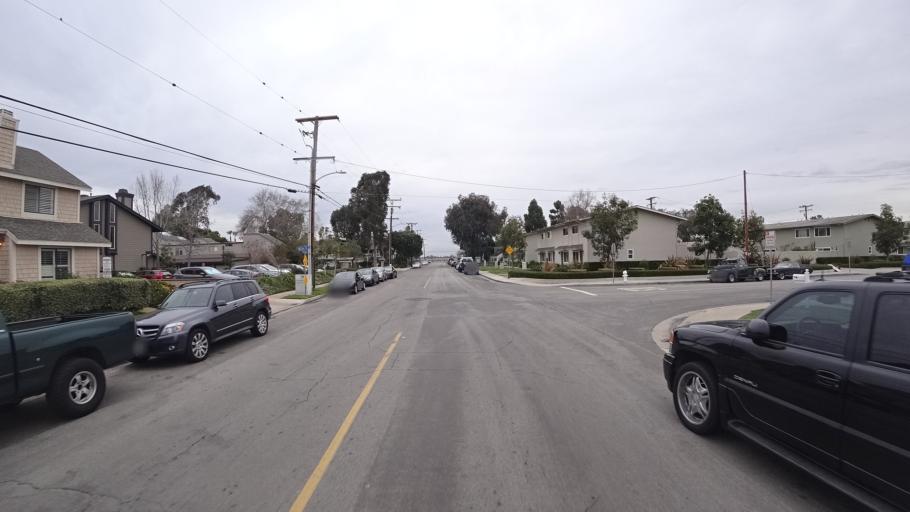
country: US
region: California
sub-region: Orange County
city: Costa Mesa
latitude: 33.6560
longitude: -117.9435
